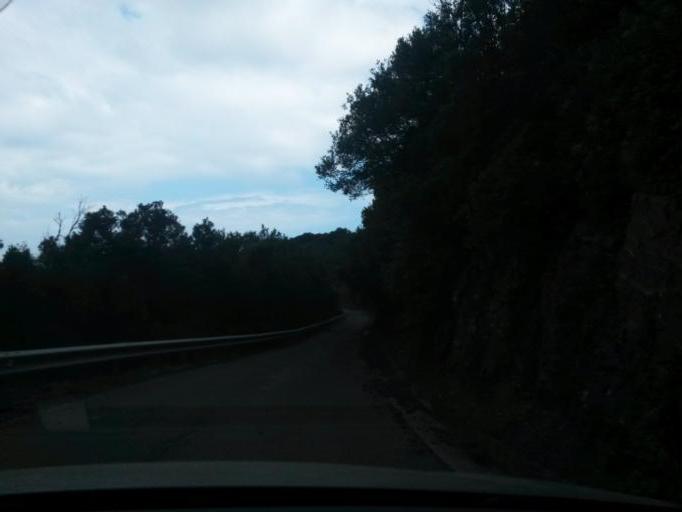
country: IT
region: Tuscany
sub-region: Provincia di Livorno
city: Rio nell'Elba
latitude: 42.8249
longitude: 10.3920
